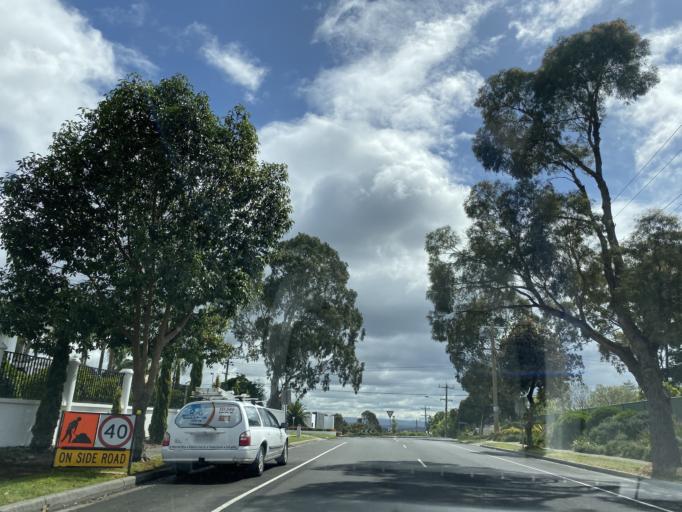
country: AU
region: Victoria
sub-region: Manningham
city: Doncaster East
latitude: -37.7661
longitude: 145.1416
